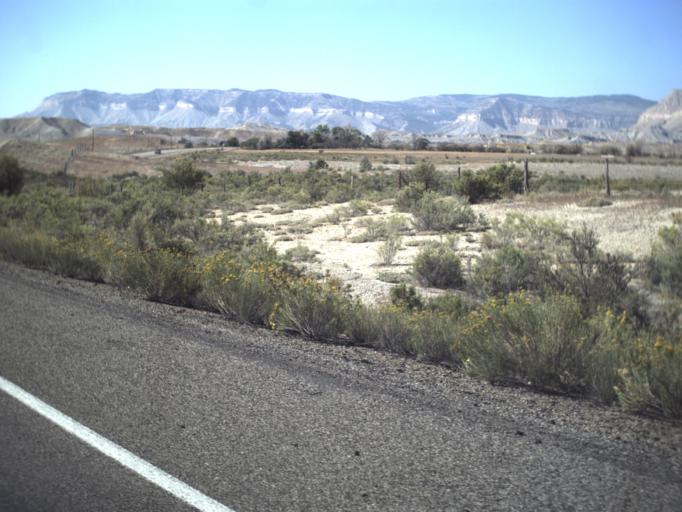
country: US
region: Utah
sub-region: Emery County
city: Castle Dale
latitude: 39.1748
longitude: -111.0507
